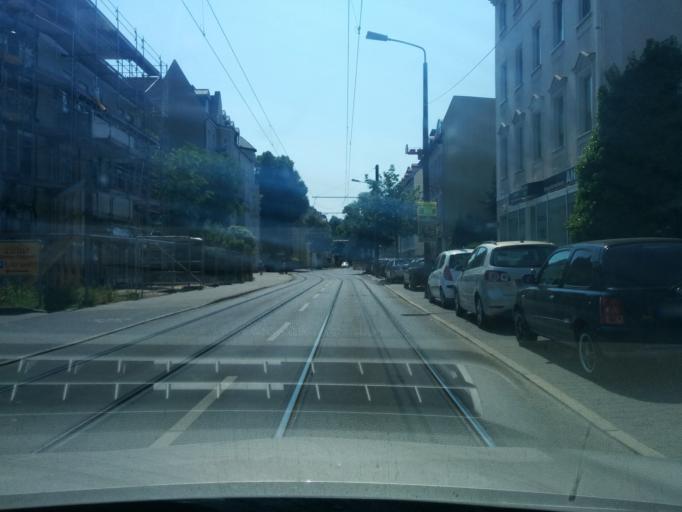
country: DE
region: Berlin
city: Grunau
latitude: 52.4175
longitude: 13.5804
